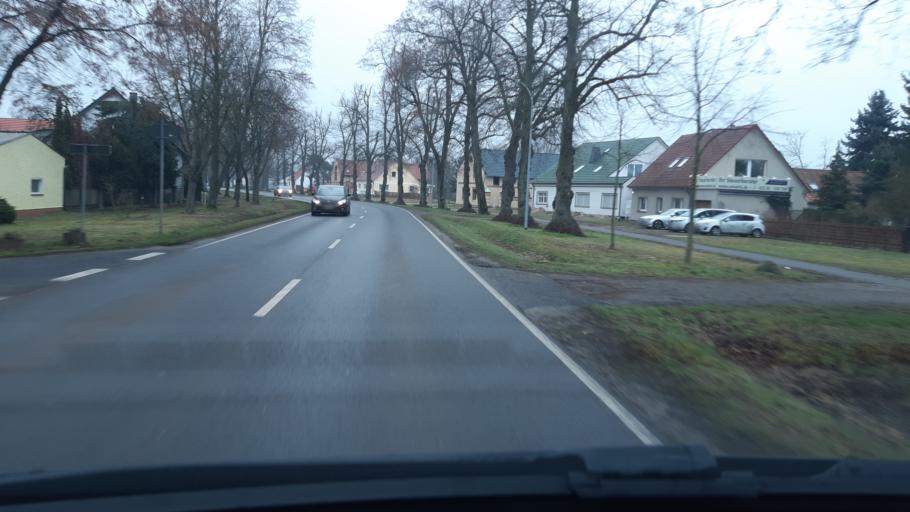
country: DE
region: Brandenburg
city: Leegebruch
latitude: 52.7480
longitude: 13.1811
